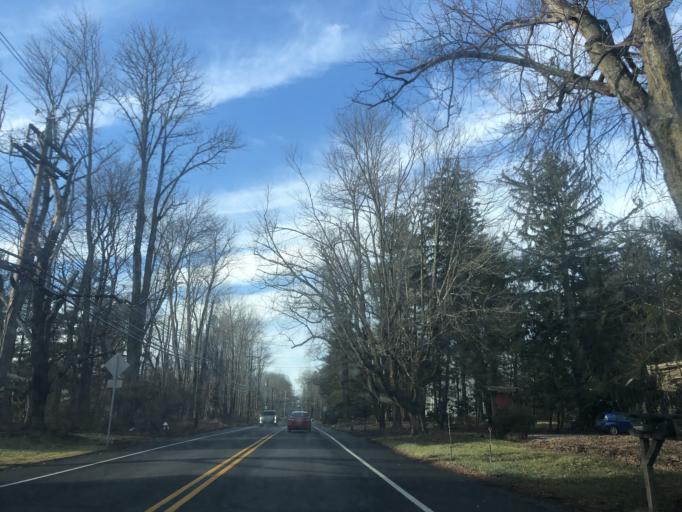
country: US
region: New Jersey
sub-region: Somerset County
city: Kingston
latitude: 40.3786
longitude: -74.6073
